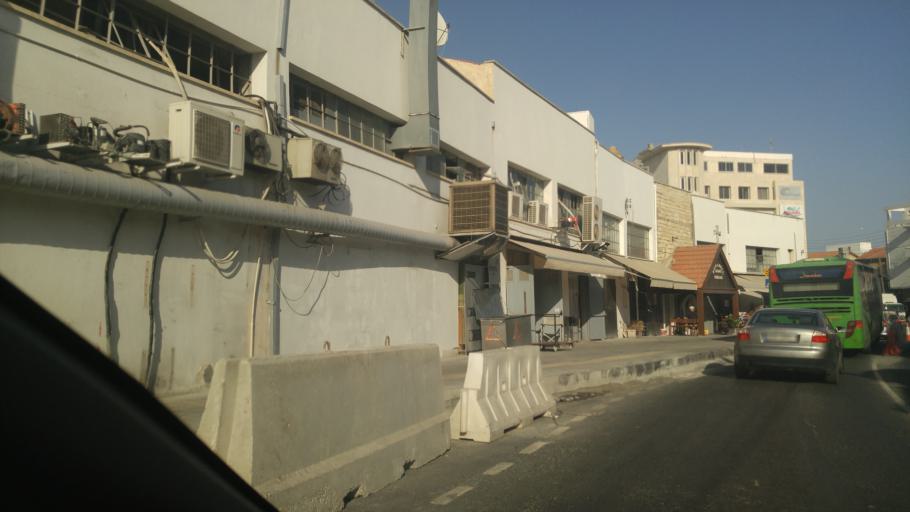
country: CY
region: Limassol
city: Limassol
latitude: 34.6717
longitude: 33.0415
